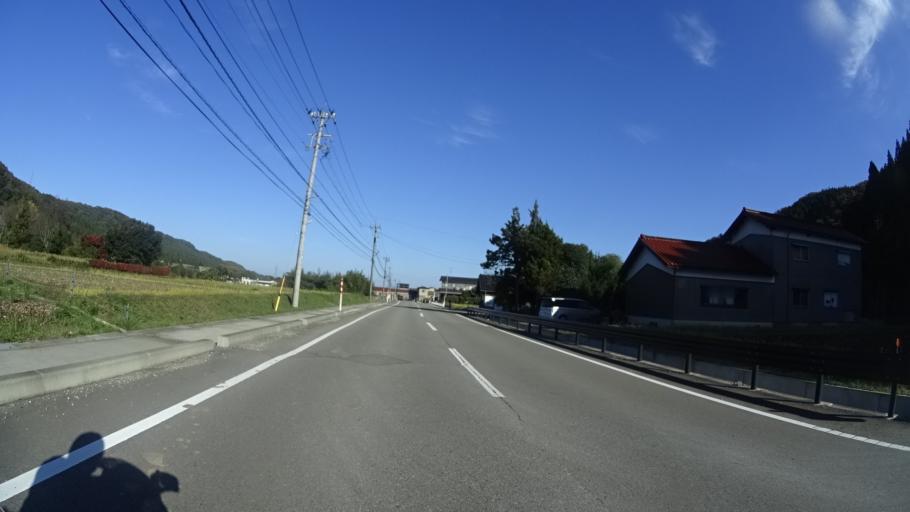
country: JP
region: Ishikawa
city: Komatsu
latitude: 36.2732
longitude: 136.3938
